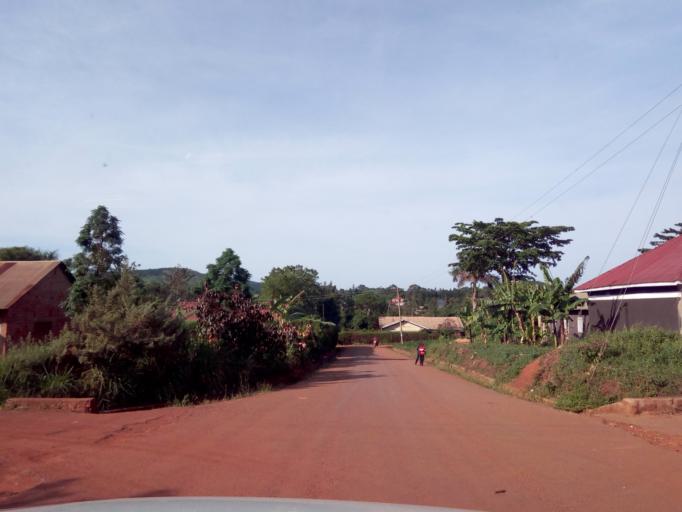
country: UG
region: Western Region
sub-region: Masindi District
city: Masindi
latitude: 1.6786
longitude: 31.7216
